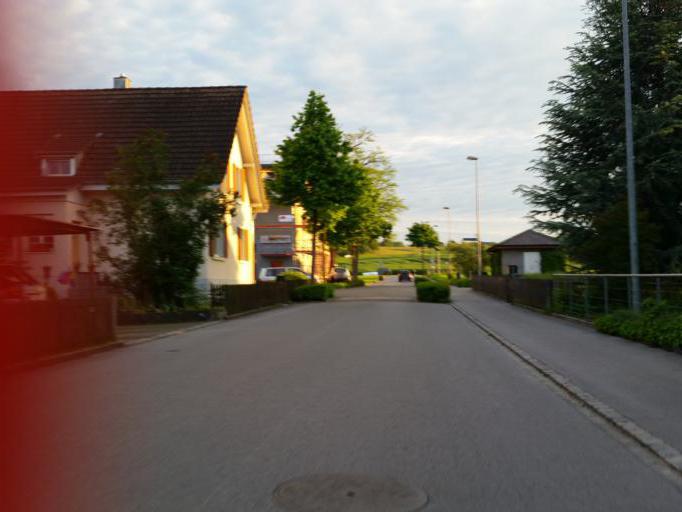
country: CH
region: Thurgau
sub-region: Arbon District
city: Amriswil
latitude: 47.5425
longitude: 9.2900
